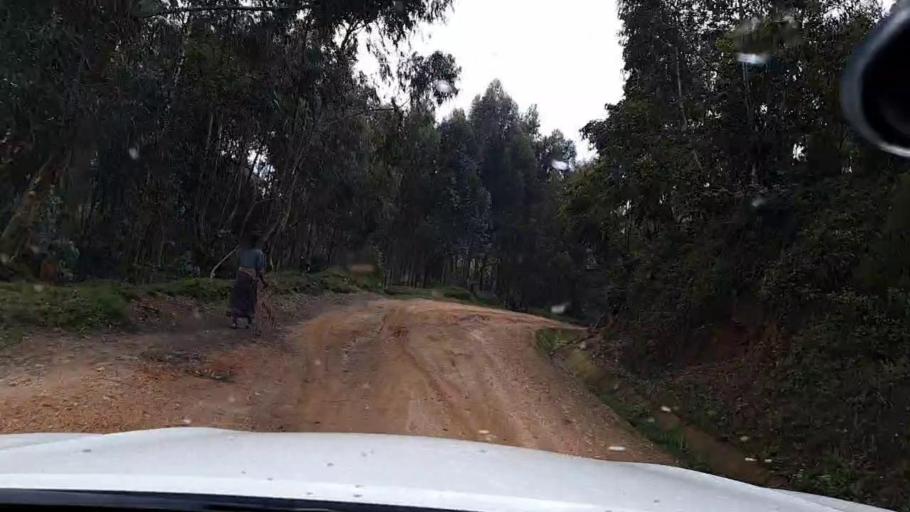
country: RW
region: Western Province
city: Kibuye
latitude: -2.2518
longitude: 29.3460
